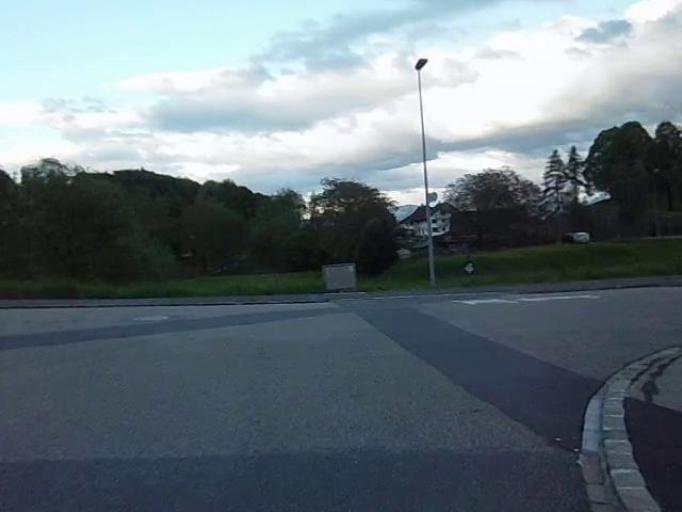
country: CH
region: Zurich
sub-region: Bezirk Hinwil
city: Rueti / Oberdorf
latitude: 47.2528
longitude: 8.8703
